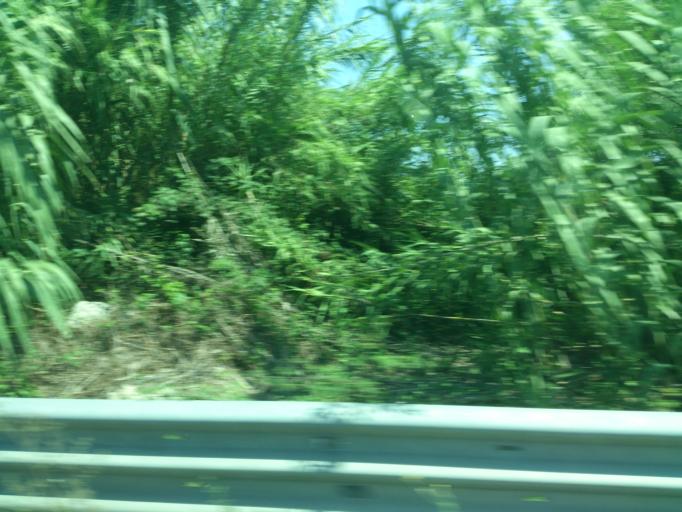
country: IT
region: Calabria
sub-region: Provincia di Reggio Calabria
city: Rosarno
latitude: 38.4672
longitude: 16.0090
